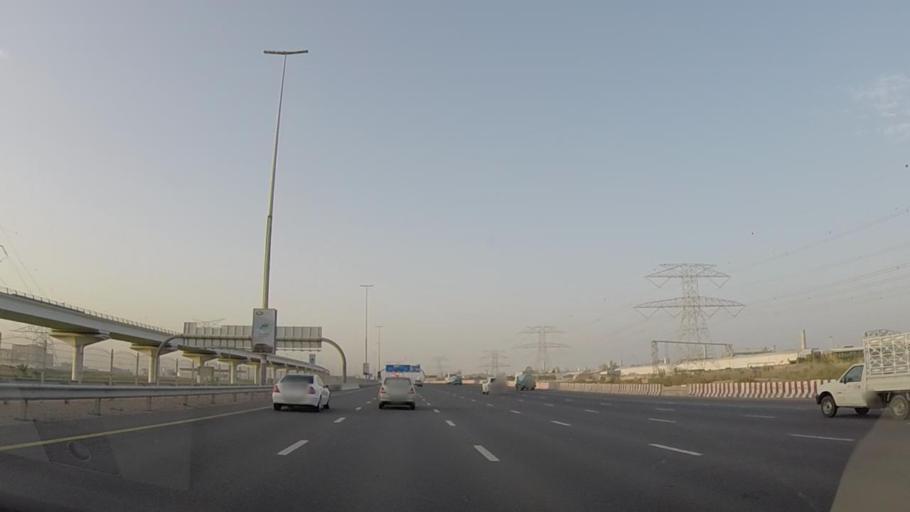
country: AE
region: Dubai
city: Dubai
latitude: 25.0355
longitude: 55.1068
